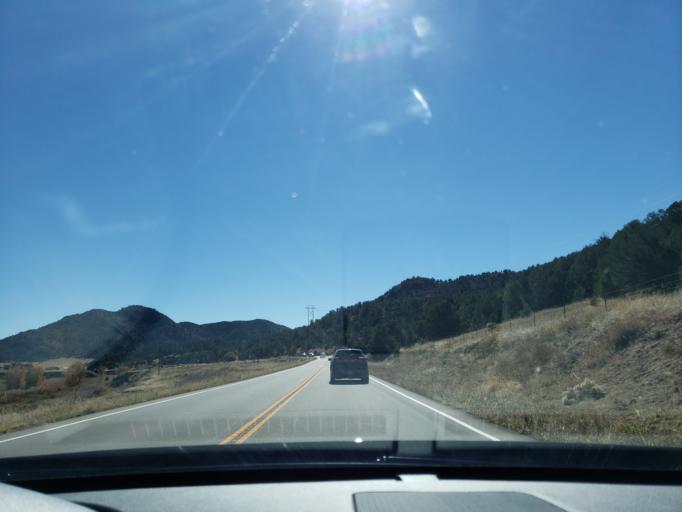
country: US
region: Colorado
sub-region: Fremont County
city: Canon City
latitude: 38.5929
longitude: -105.4247
